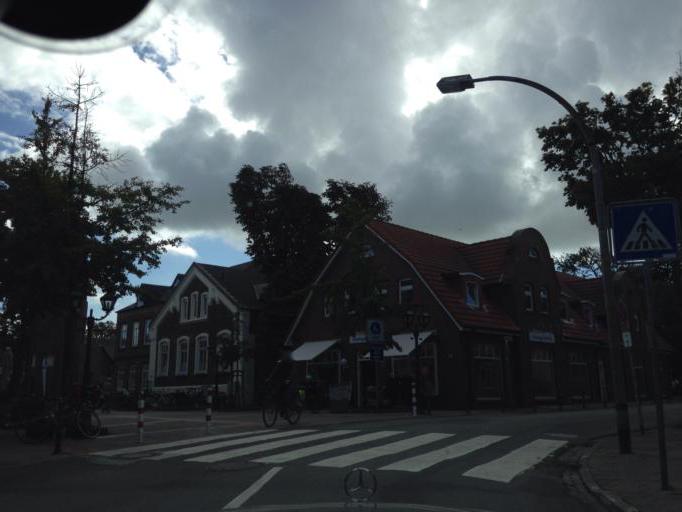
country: DE
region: Schleswig-Holstein
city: Wyk auf Fohr
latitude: 54.6910
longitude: 8.5671
